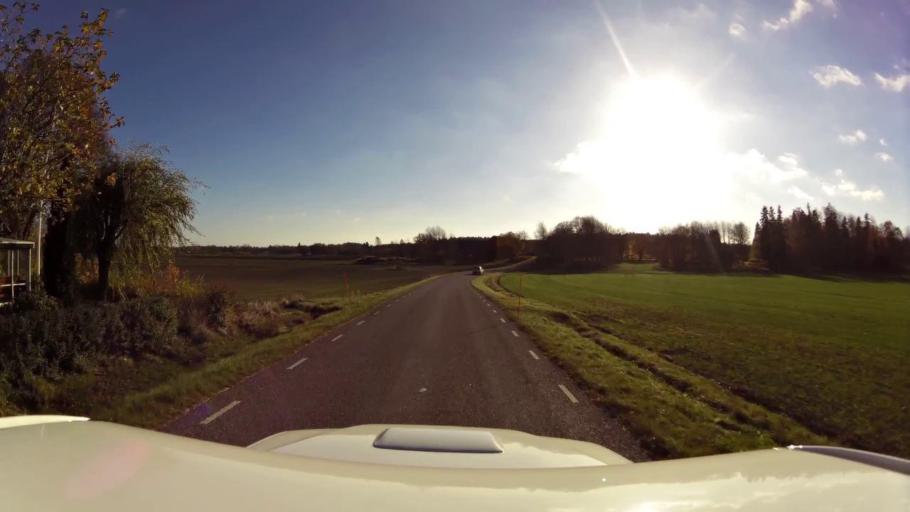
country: SE
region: OEstergoetland
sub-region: Linkopings Kommun
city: Linghem
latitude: 58.4652
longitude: 15.7712
